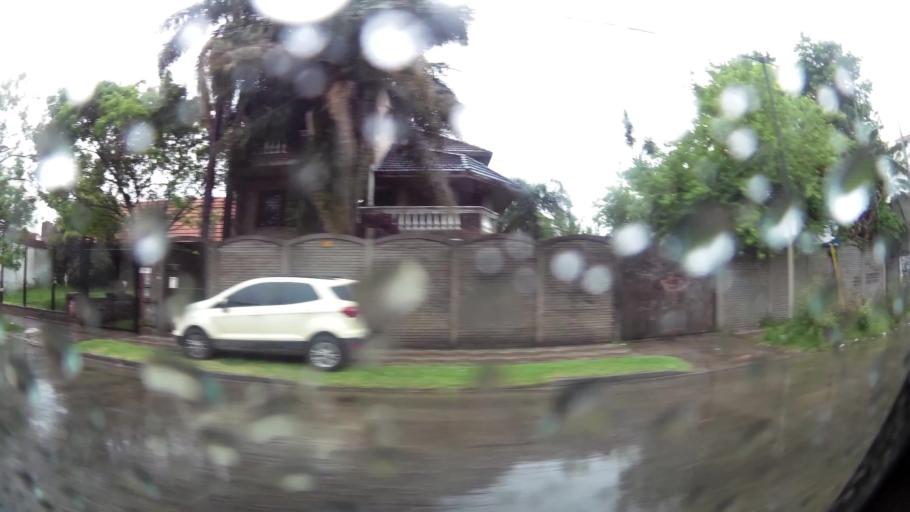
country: AR
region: Buenos Aires
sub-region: Partido de Lanus
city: Lanus
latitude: -34.7054
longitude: -58.4076
